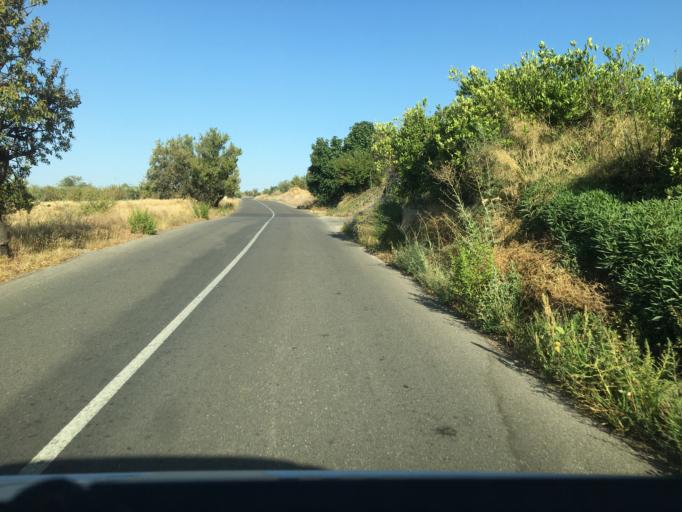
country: ES
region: Andalusia
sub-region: Provincia de Almeria
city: Huercal-Overa
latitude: 37.4702
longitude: -1.8983
